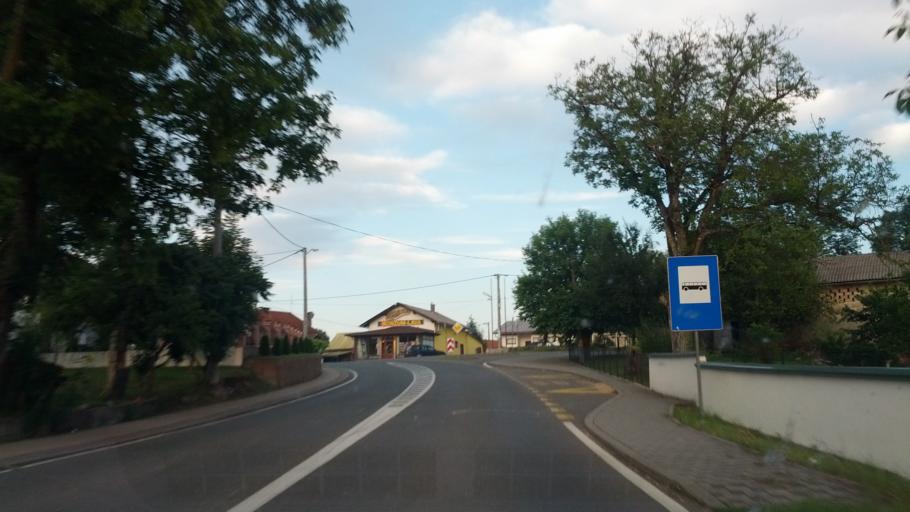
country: BA
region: Federation of Bosnia and Herzegovina
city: Izacic
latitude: 44.8787
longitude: 15.7745
